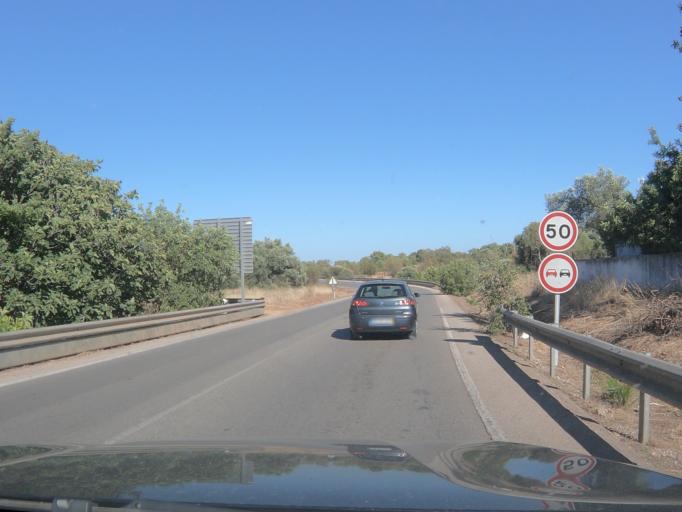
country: PT
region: Faro
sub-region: Loule
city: Almancil
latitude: 37.1031
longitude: -8.0563
